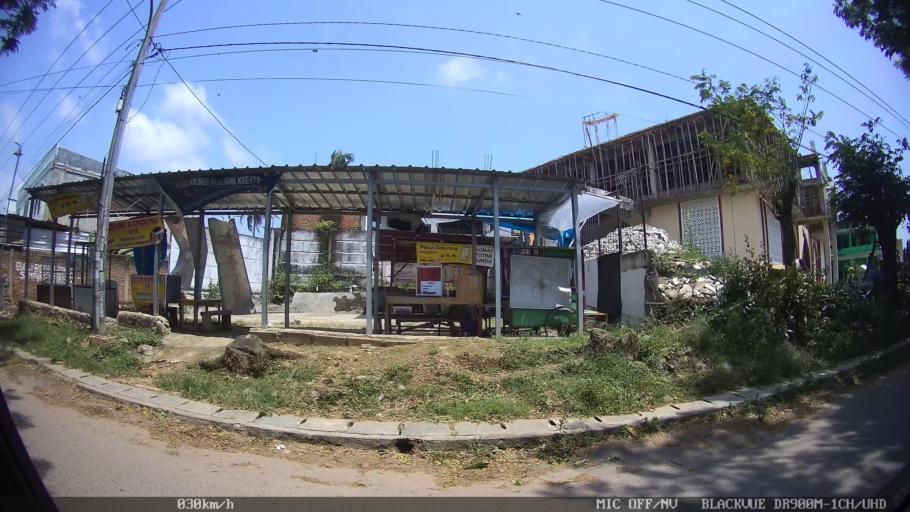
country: ID
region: Lampung
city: Kedaton
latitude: -5.3611
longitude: 105.2698
